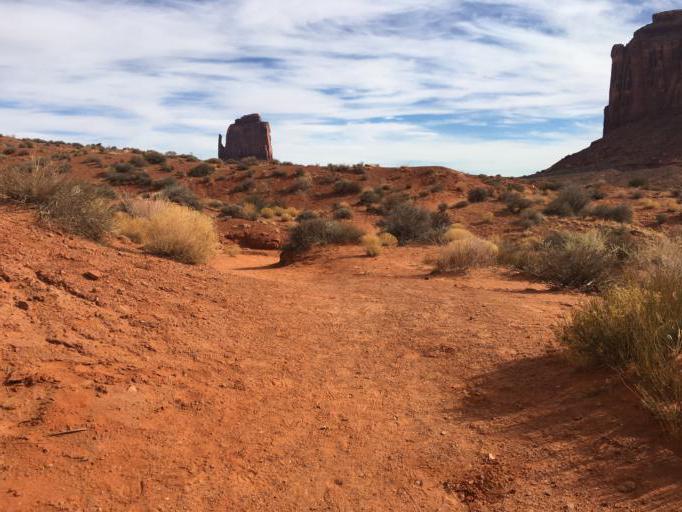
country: US
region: Arizona
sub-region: Navajo County
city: Kayenta
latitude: 36.9863
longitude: -110.0973
